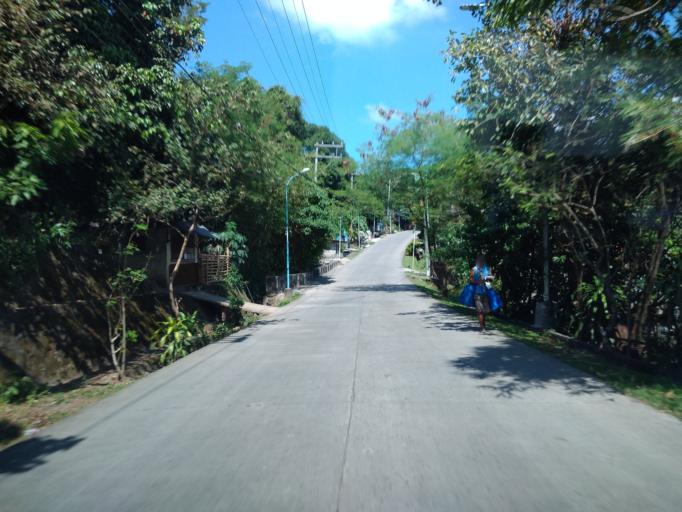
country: PH
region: Central Luzon
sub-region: Province of Bulacan
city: San Jose del Monte
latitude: 14.8478
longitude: 121.0713
